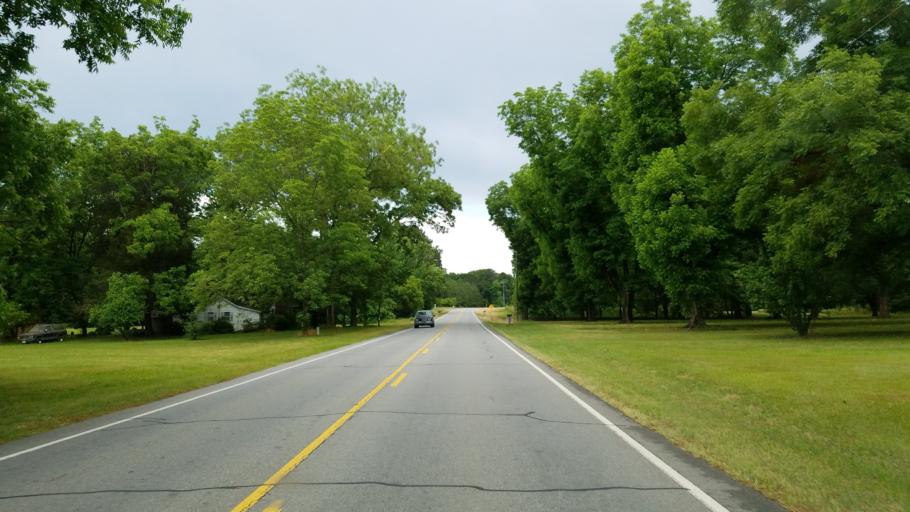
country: US
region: Georgia
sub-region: Dooly County
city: Vienna
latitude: 32.1382
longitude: -83.7968
